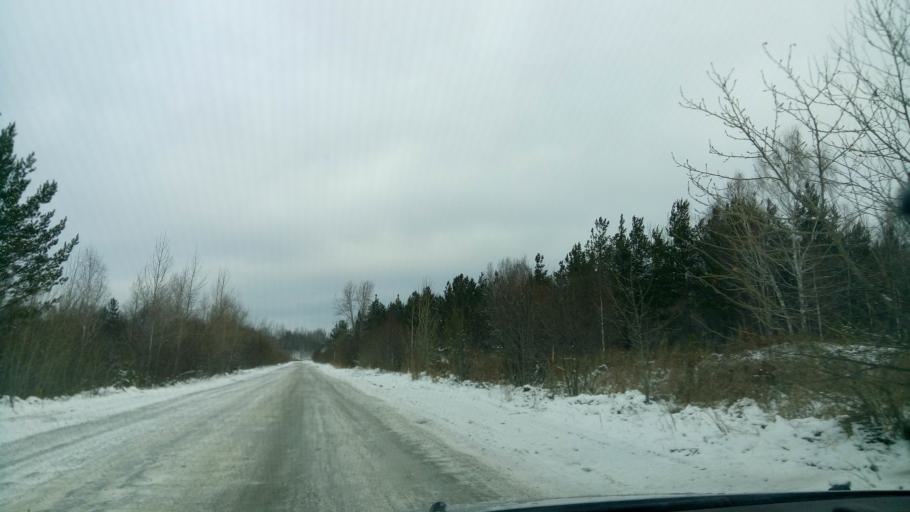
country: RU
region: Sverdlovsk
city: Polevskoy
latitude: 56.4578
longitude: 60.1836
